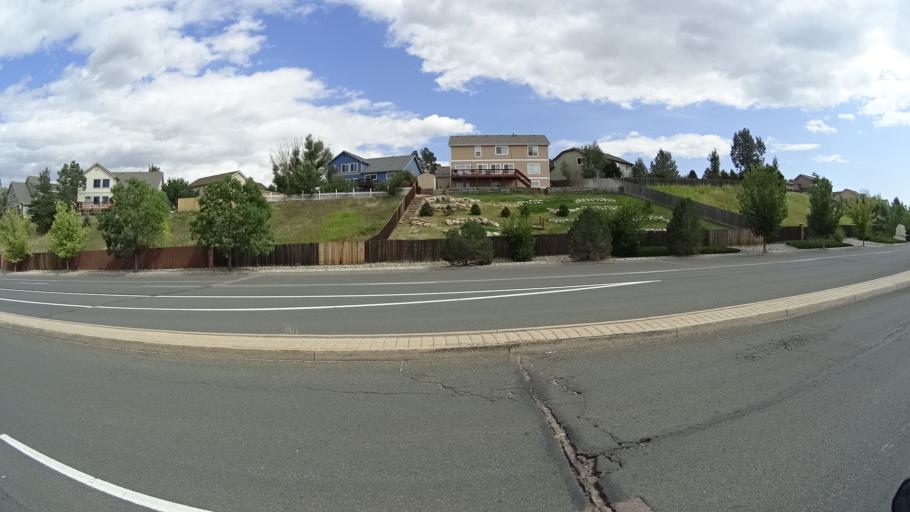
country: US
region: Colorado
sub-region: El Paso County
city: Cimarron Hills
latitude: 38.9016
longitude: -104.6968
